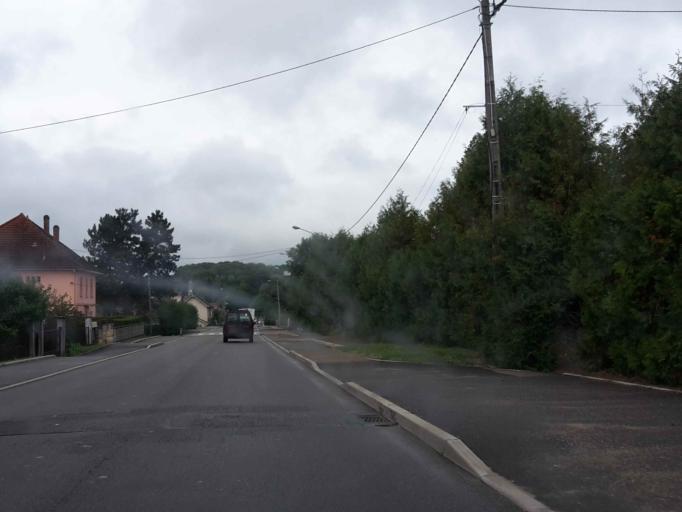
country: FR
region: Franche-Comte
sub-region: Departement du Doubs
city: Roulans
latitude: 47.3176
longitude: 6.2390
